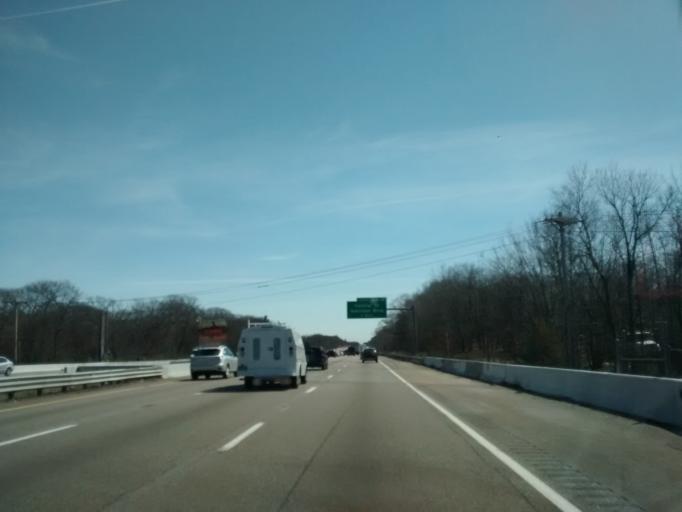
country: US
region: Massachusetts
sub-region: Norfolk County
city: Avon
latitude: 42.1442
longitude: -71.0664
